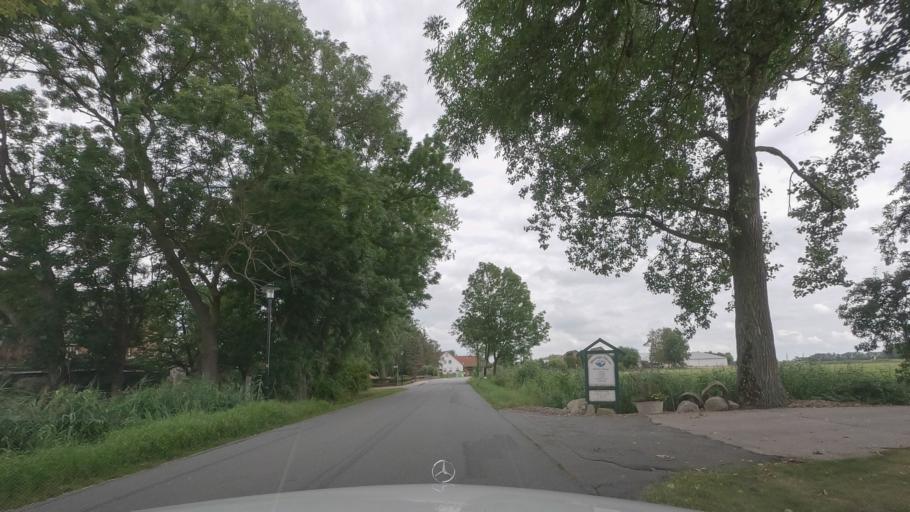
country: DE
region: Lower Saxony
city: Uthlede
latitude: 53.2942
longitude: 8.5301
